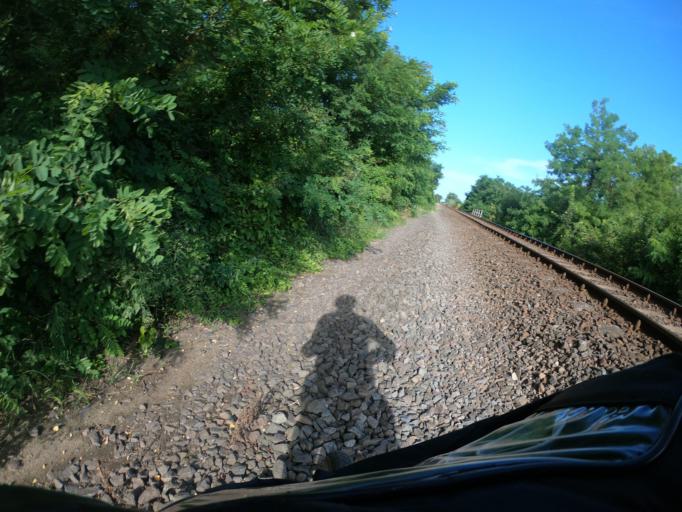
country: HU
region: Hajdu-Bihar
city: Tiszacsege
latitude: 47.6161
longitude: 21.0133
